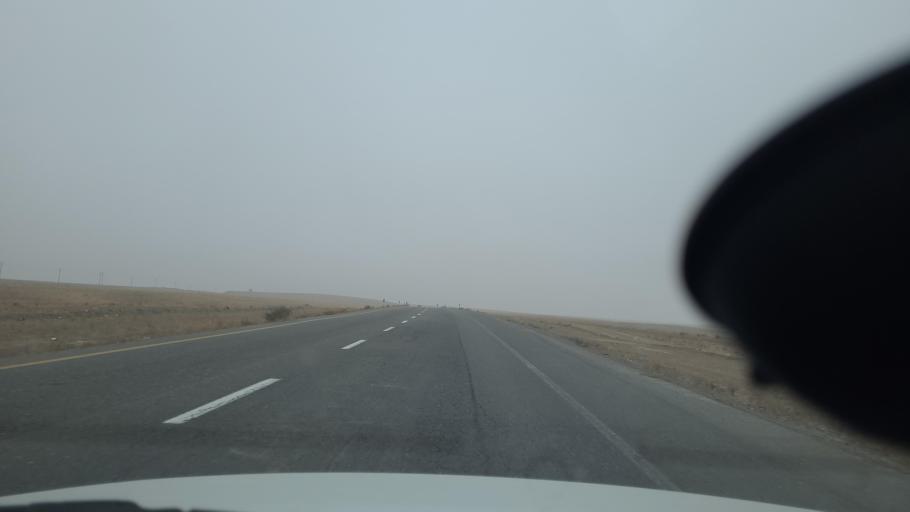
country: IR
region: Razavi Khorasan
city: Fariman
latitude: 35.8618
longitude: 59.7591
